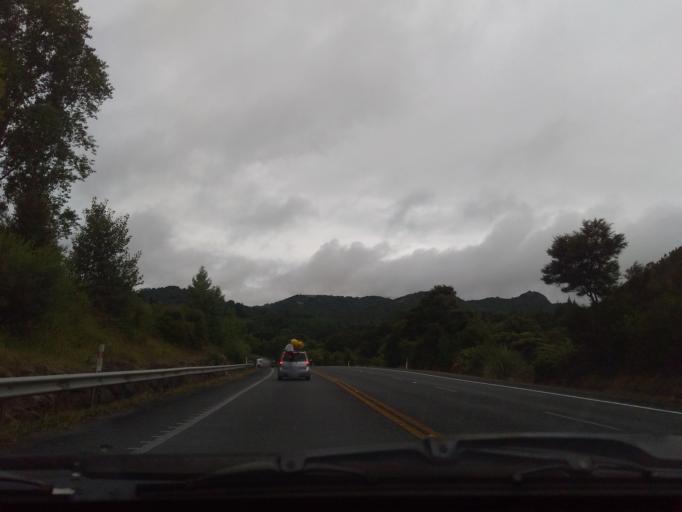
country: NZ
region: Auckland
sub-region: Auckland
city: Wellsford
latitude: -36.1313
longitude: 174.4303
